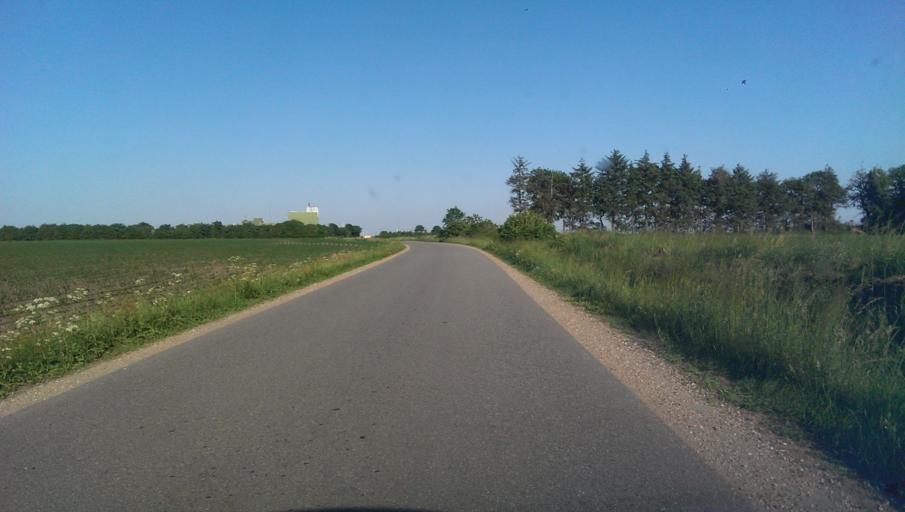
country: DK
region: South Denmark
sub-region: Esbjerg Kommune
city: Bramming
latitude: 55.5490
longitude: 8.6466
